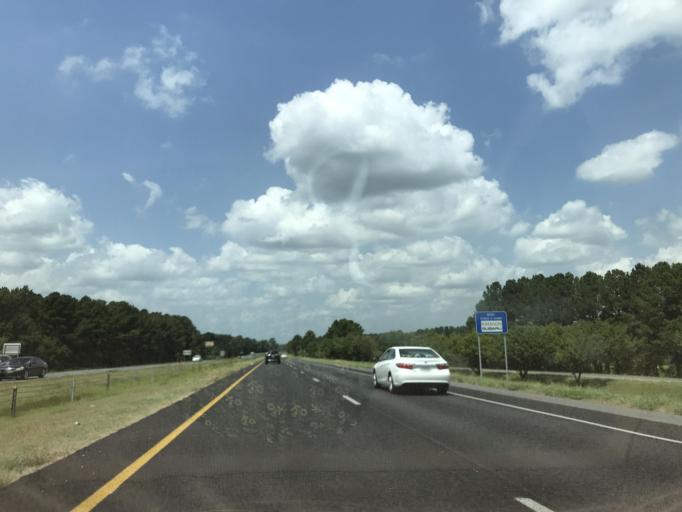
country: US
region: North Carolina
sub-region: Duplin County
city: Wallace
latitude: 34.7703
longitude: -77.9655
